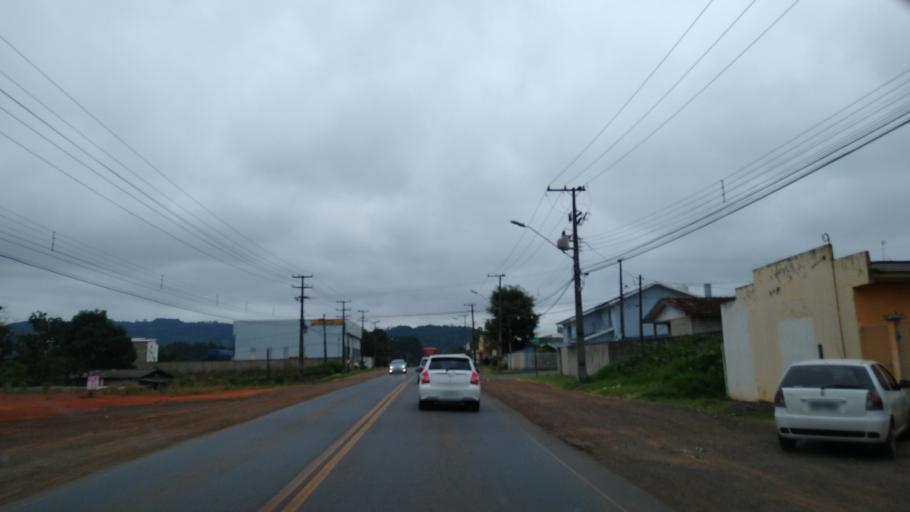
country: BR
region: Parana
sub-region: Uniao Da Vitoria
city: Uniao da Vitoria
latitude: -26.2448
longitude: -51.1222
